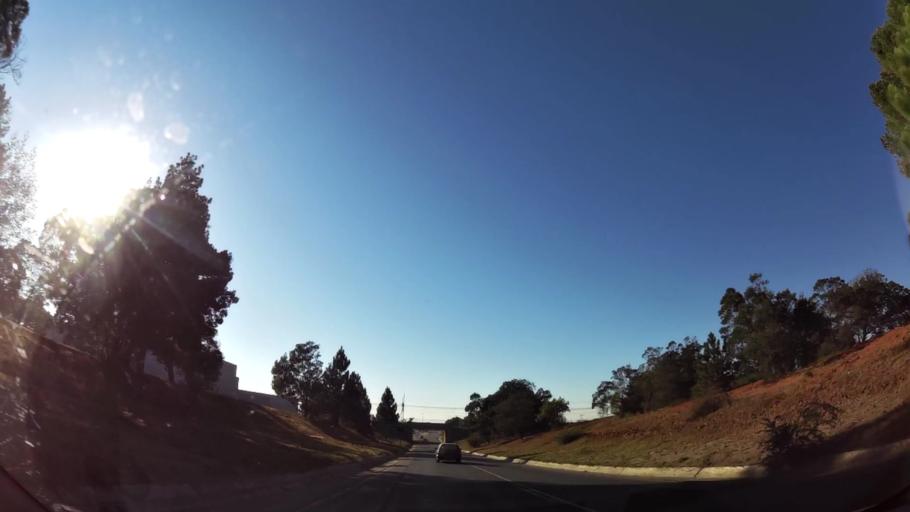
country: ZA
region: Gauteng
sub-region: Ekurhuleni Metropolitan Municipality
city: Tembisa
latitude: -26.0395
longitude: 28.2526
